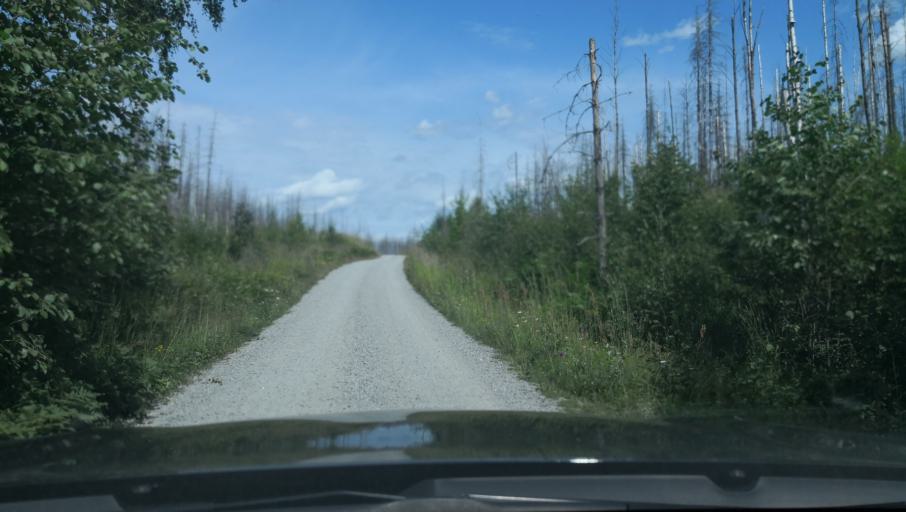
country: SE
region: Vaestmanland
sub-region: Surahammars Kommun
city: Ramnas
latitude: 59.8985
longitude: 16.1077
